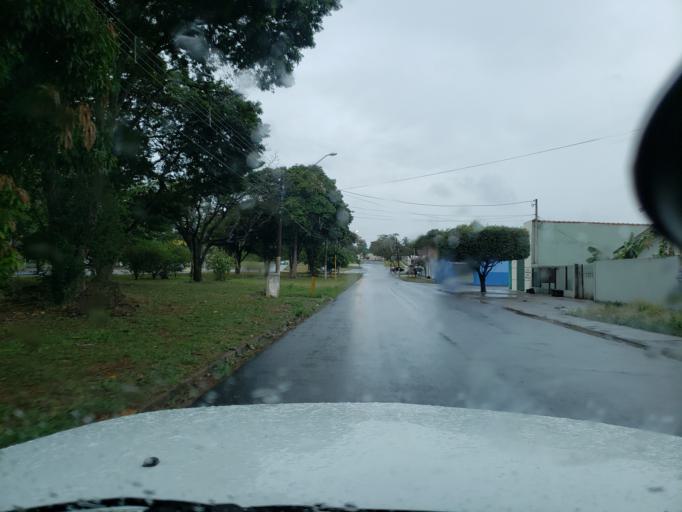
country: BR
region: Sao Paulo
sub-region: Moji-Guacu
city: Mogi-Gaucu
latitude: -22.3493
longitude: -46.9396
